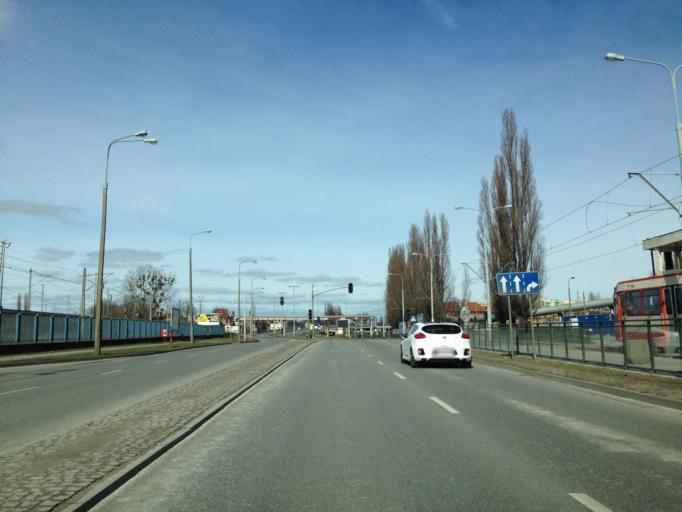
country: PL
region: Pomeranian Voivodeship
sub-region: Gdansk
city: Gdansk
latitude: 54.3716
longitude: 18.6338
